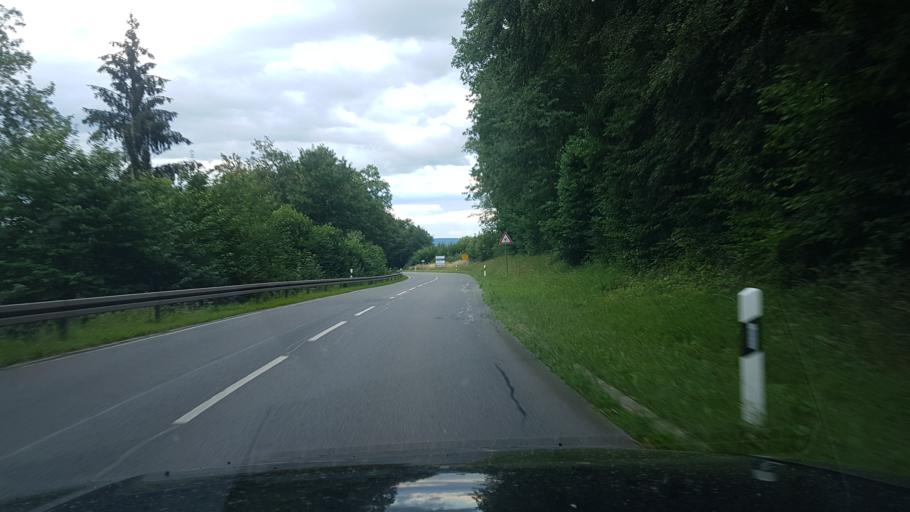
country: DE
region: Baden-Wuerttemberg
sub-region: Freiburg Region
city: Donaueschingen
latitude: 47.9565
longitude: 8.4775
